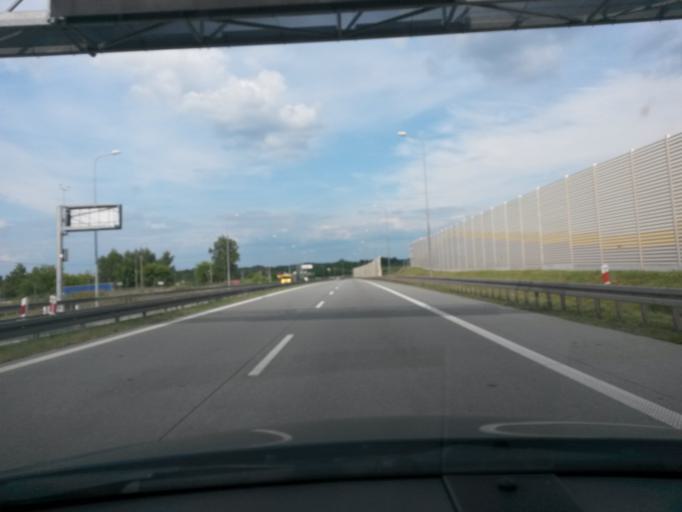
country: PL
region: Lodz Voivodeship
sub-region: Powiat skierniewicki
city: Kowiesy
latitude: 51.8828
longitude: 20.4077
